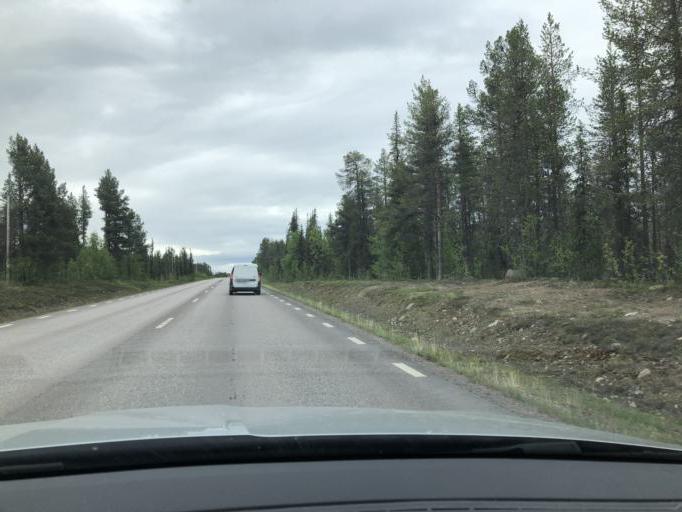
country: SE
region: Norrbotten
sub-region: Kiruna Kommun
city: Kiruna
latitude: 67.8294
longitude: 20.5300
